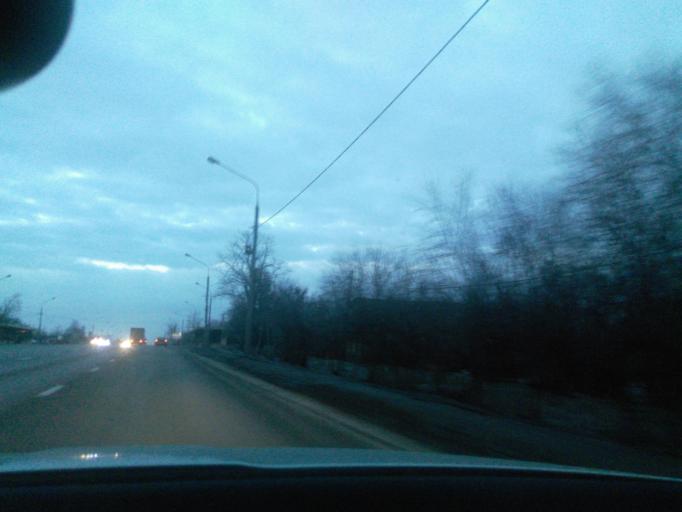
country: RU
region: Moskovskaya
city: Novopodrezkovo
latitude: 55.9269
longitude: 37.3837
